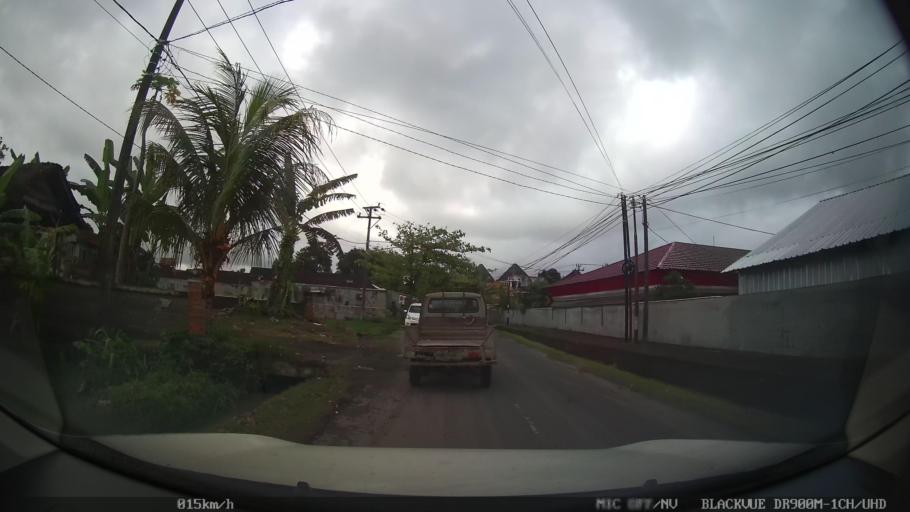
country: ID
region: Bali
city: Banjar Mambalkajanan
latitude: -8.5447
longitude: 115.2139
